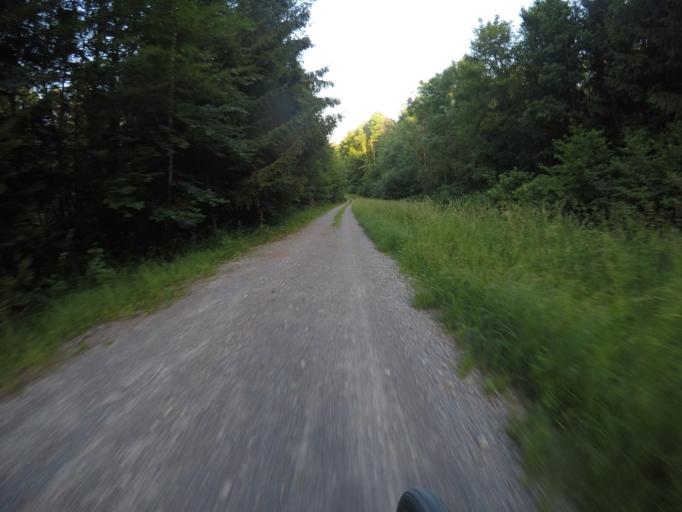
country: DE
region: Baden-Wuerttemberg
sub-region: Regierungsbezirk Stuttgart
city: Schonaich
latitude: 48.6711
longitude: 9.0569
